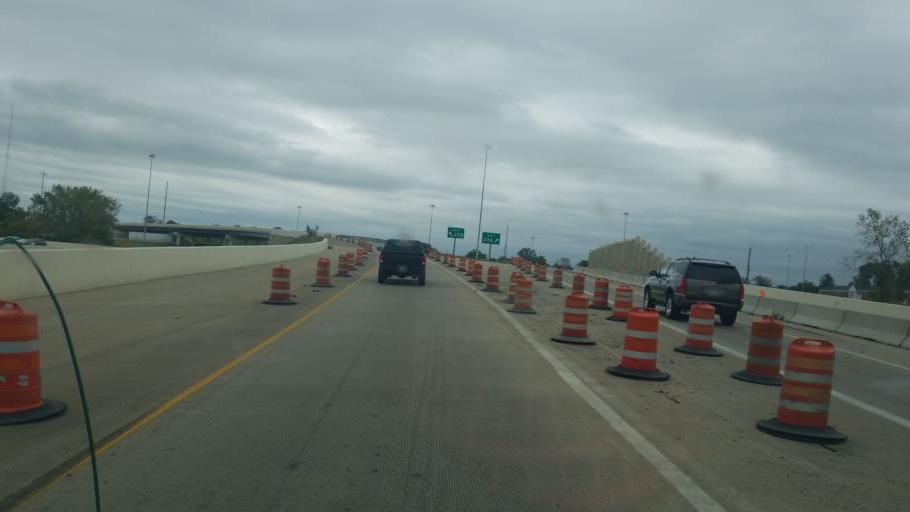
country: US
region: Ohio
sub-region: Lucas County
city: Toledo
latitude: 41.6754
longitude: -83.5779
